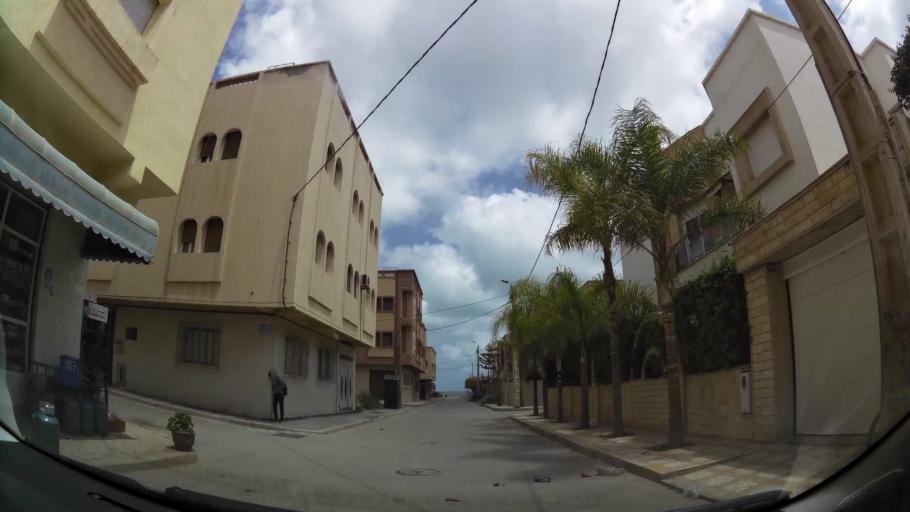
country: MA
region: Oriental
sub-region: Nador
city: Nador
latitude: 35.1687
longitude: -2.9157
